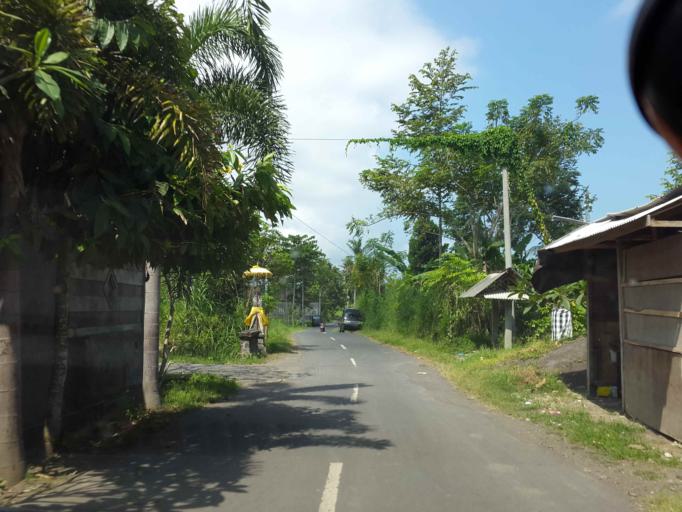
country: ID
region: Bali
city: Klungkung
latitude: -8.5441
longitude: 115.3738
